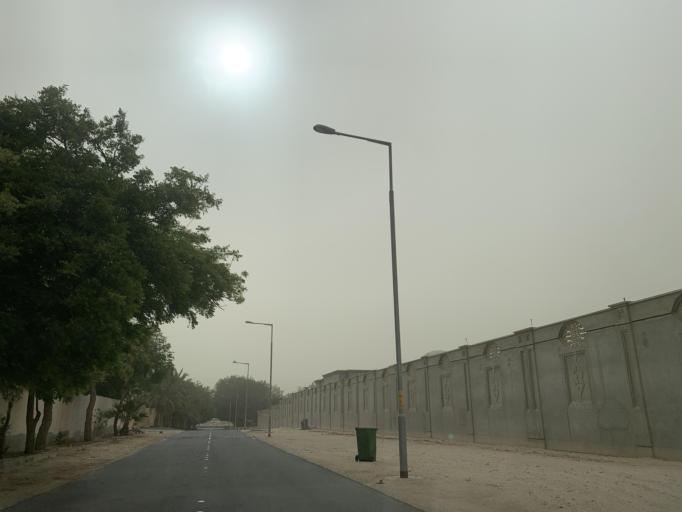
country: BH
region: Northern
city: Ar Rifa'
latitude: 26.1423
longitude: 50.5383
